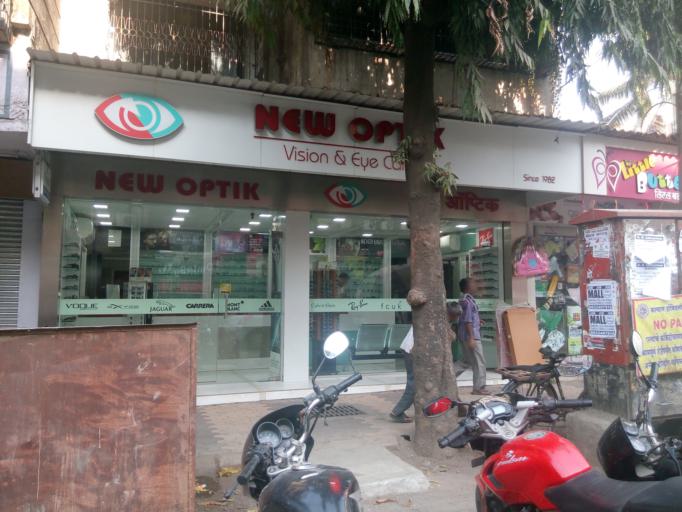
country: IN
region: Maharashtra
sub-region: Thane
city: Dombivli
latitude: 19.2155
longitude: 73.0905
